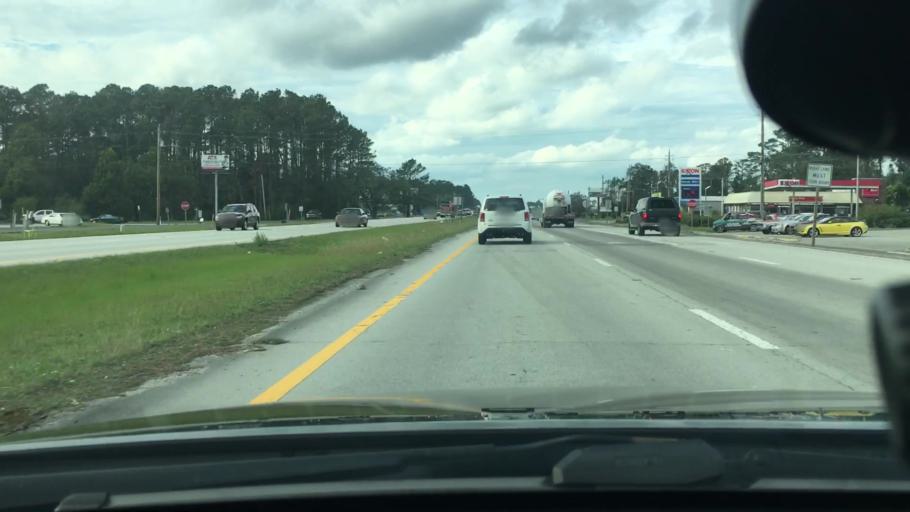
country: US
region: North Carolina
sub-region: Craven County
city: Havelock
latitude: 34.8988
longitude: -76.9291
